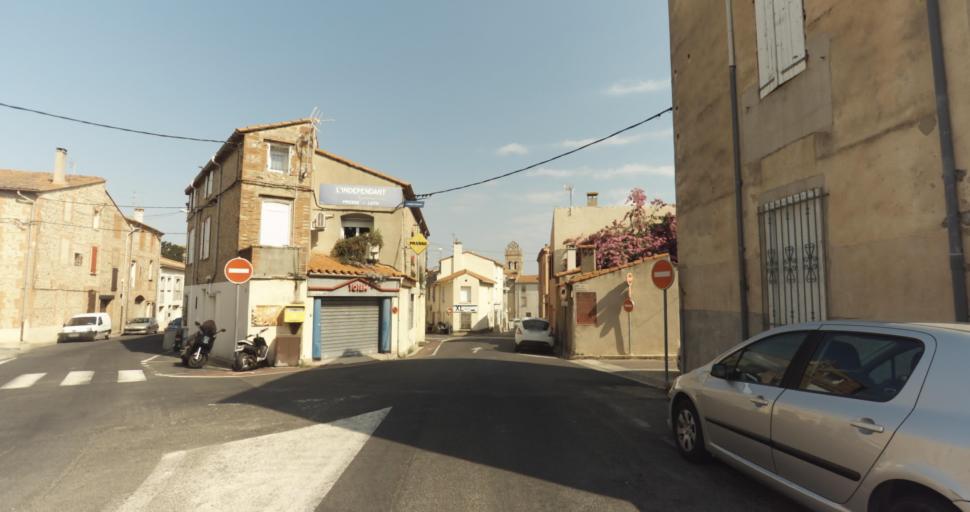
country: FR
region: Languedoc-Roussillon
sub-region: Departement des Pyrenees-Orientales
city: Latour-Bas-Elne
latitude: 42.6164
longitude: 3.0016
